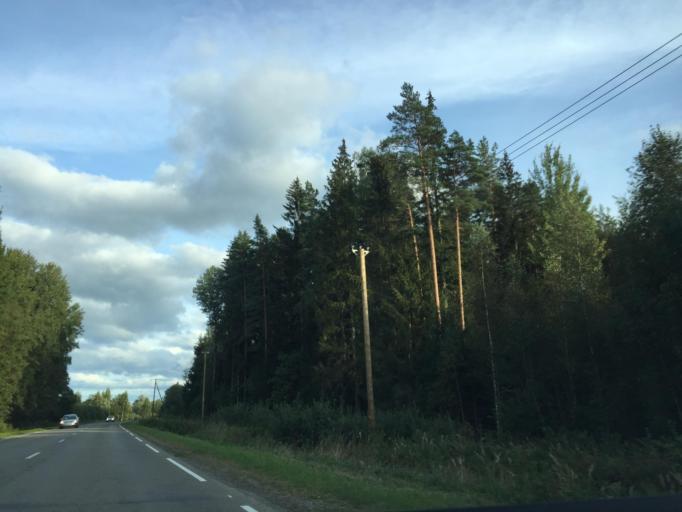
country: LV
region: Nereta
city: Nereta
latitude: 56.2858
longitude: 25.1391
